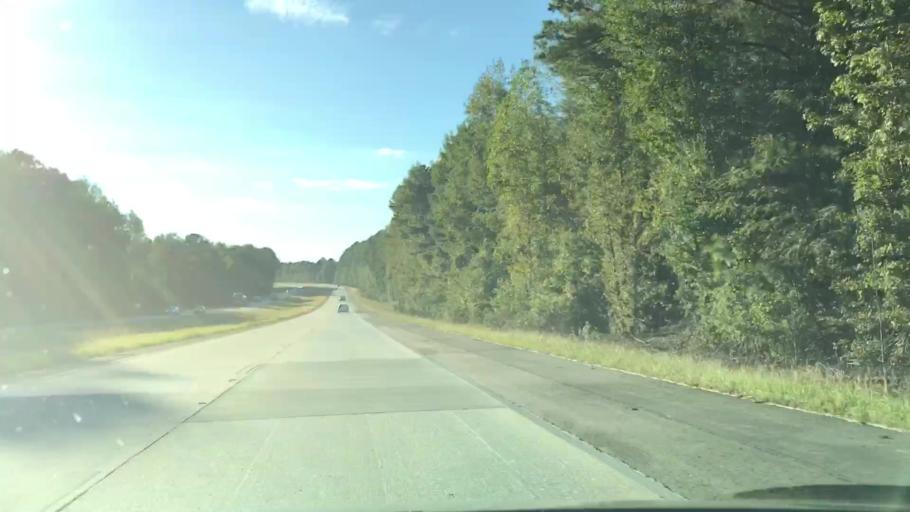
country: US
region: Georgia
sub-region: Greene County
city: Greensboro
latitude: 33.5489
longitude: -83.1249
